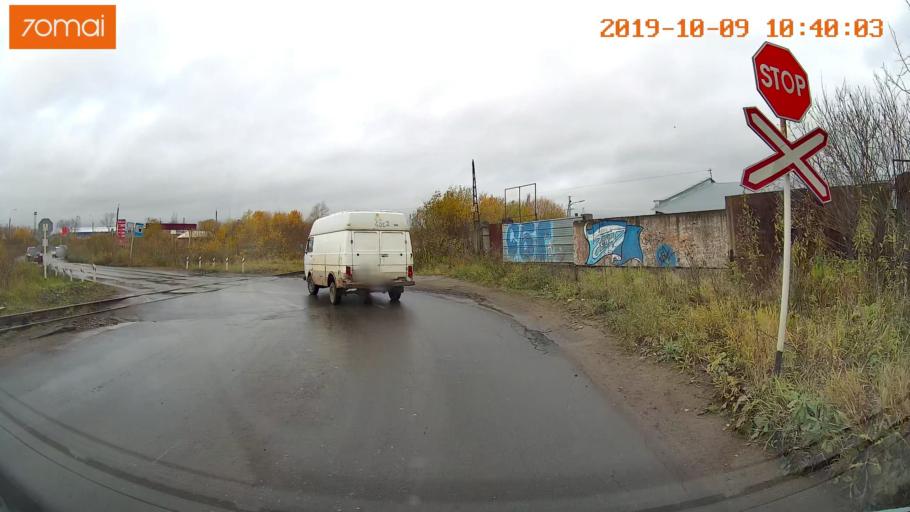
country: RU
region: Vologda
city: Vologda
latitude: 59.2335
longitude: 39.8392
